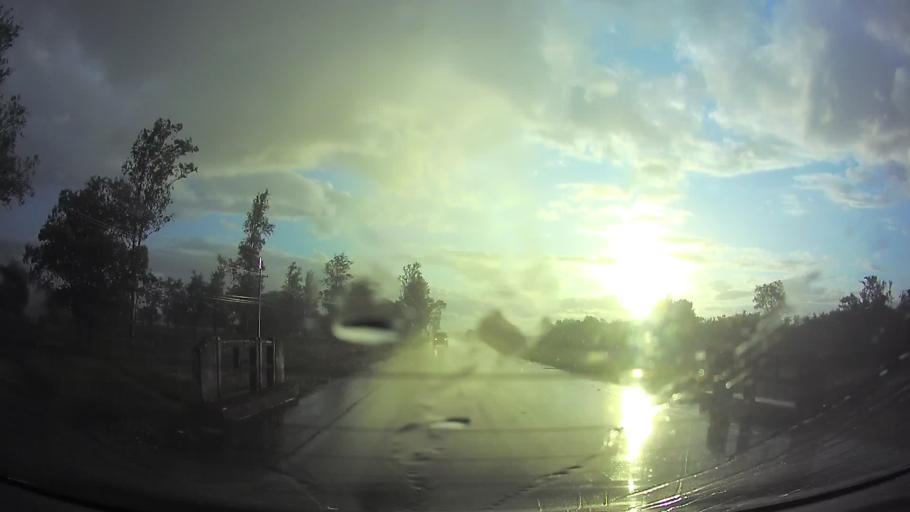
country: PY
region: Paraguari
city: Paraguari
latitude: -25.7026
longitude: -57.1804
